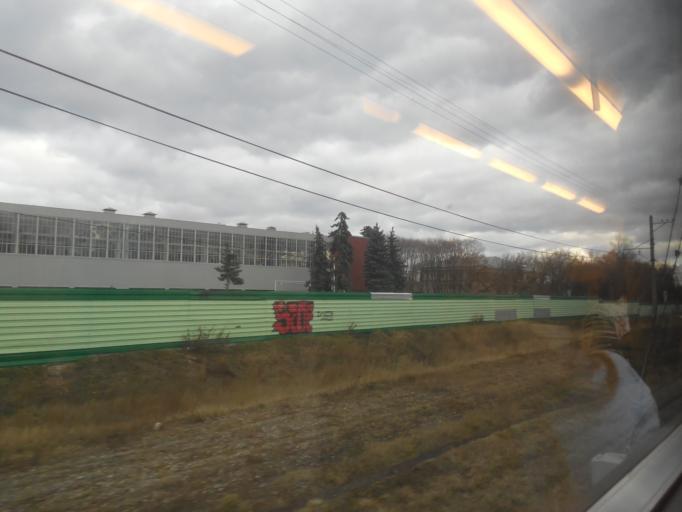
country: RU
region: Moskovskaya
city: Tomilino
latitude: 55.6629
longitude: 37.9358
